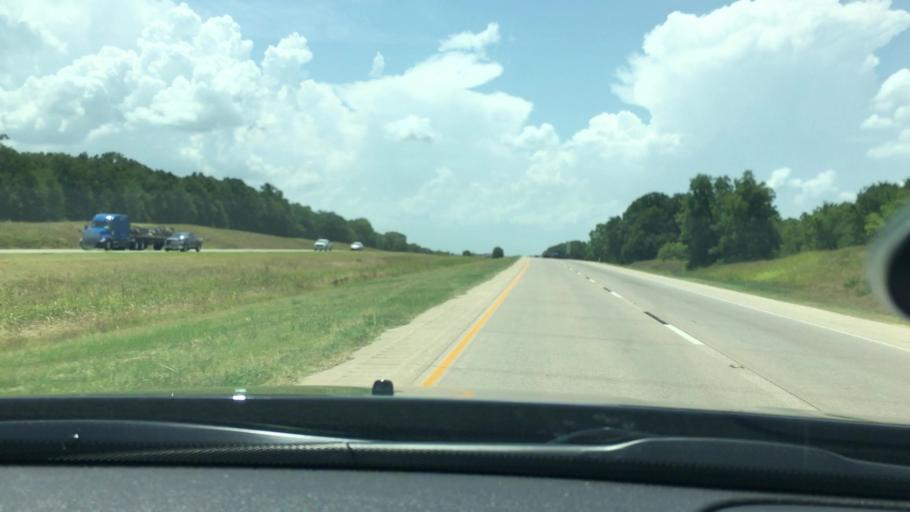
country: US
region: Oklahoma
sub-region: Carter County
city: Ardmore
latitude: 34.0645
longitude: -97.1500
